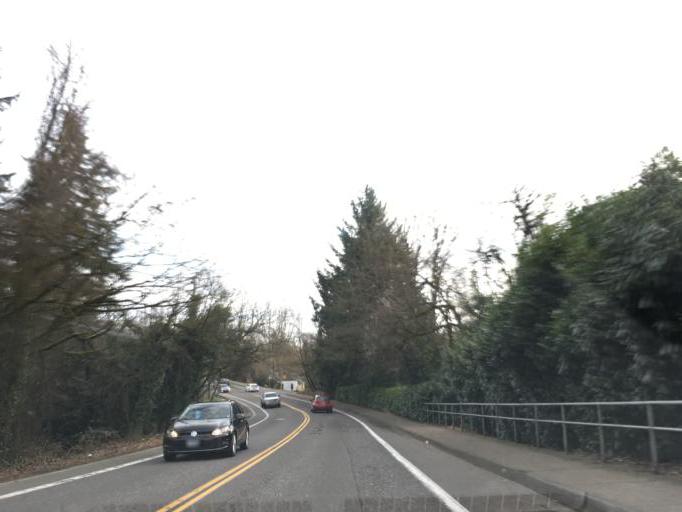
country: US
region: Oregon
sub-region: Clackamas County
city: Lake Oswego
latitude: 45.4572
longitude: -122.6850
